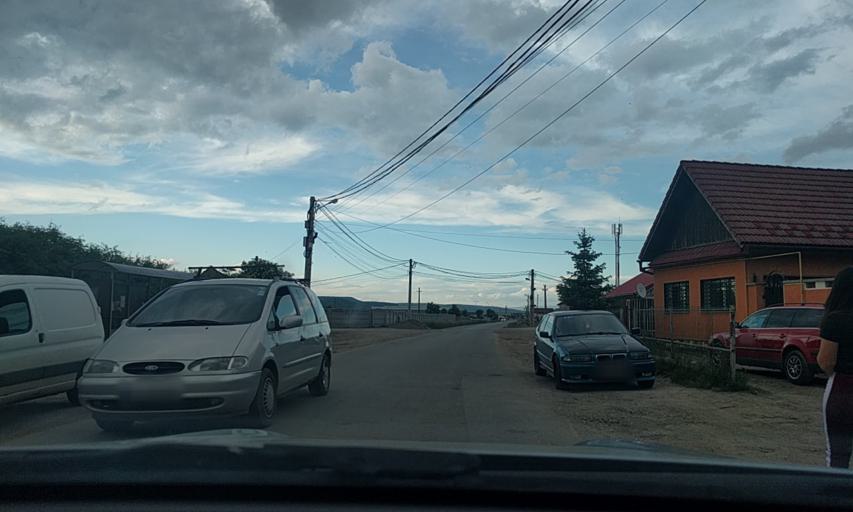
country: RO
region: Brasov
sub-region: Comuna Harman
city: Harman
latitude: 45.7183
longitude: 25.6943
